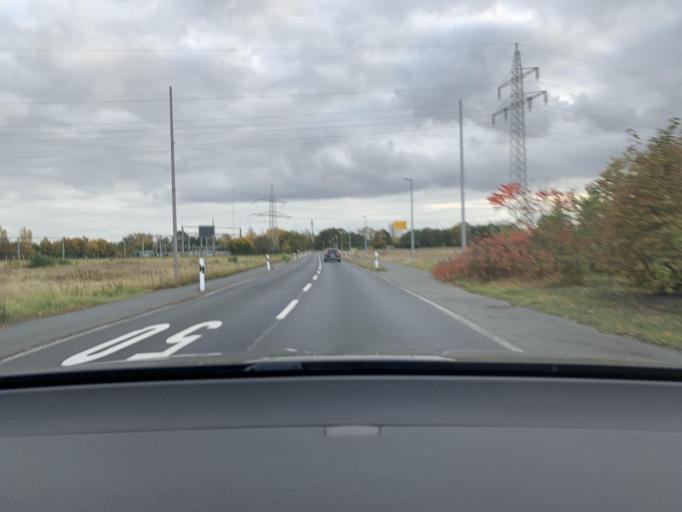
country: DE
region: Lower Saxony
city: Braunschweig
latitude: 52.3039
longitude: 10.5028
